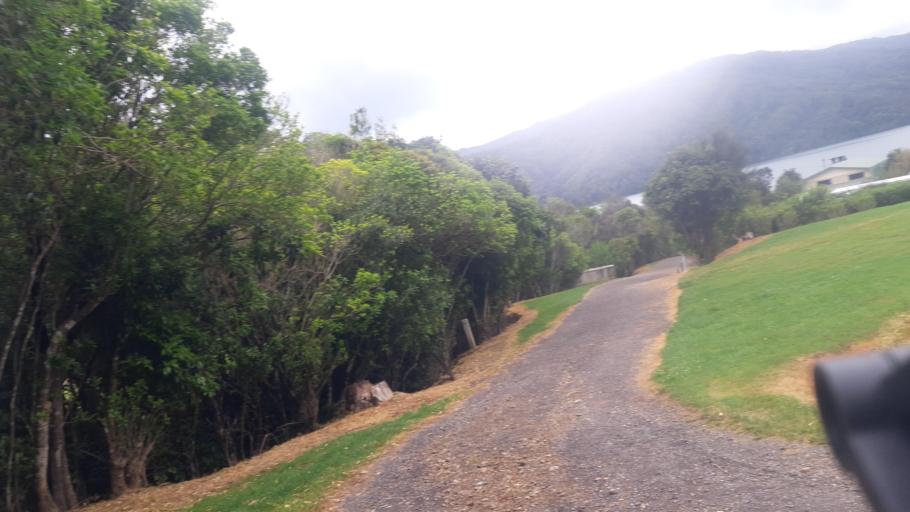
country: NZ
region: Marlborough
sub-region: Marlborough District
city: Picton
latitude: -41.2720
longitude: 173.9419
